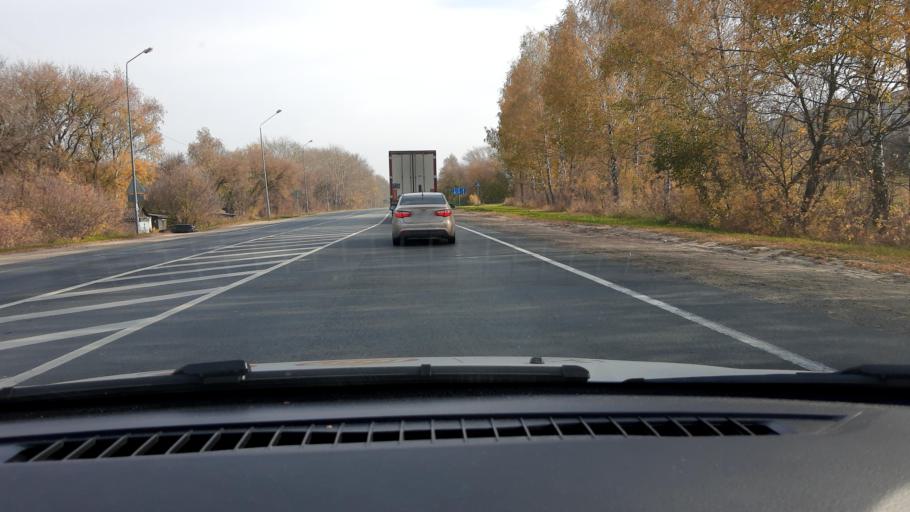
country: RU
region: Nizjnij Novgorod
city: Pamyat' Parizhskoy Kommuny
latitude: 56.0422
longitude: 44.4457
